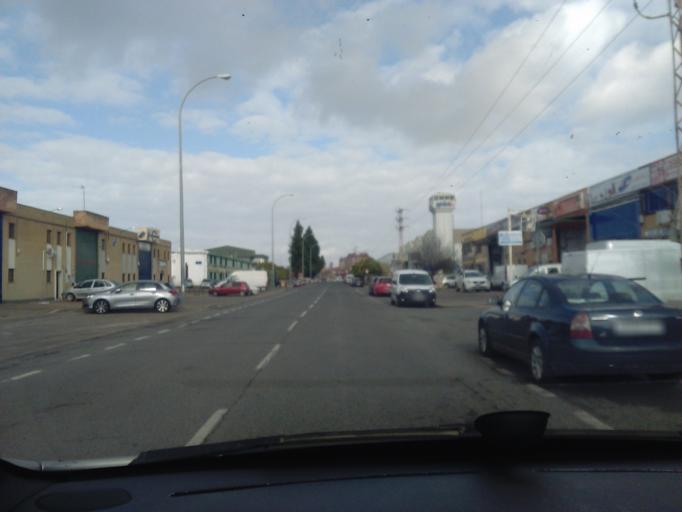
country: ES
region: Andalusia
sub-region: Provincia de Sevilla
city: Sevilla
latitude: 37.3796
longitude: -5.9250
